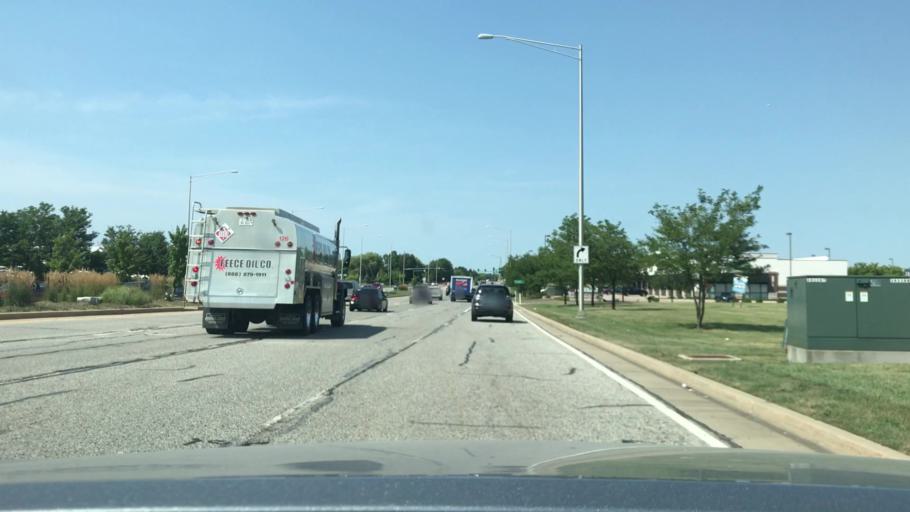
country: US
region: Illinois
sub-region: Kane County
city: North Aurora
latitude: 41.8140
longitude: -88.2795
